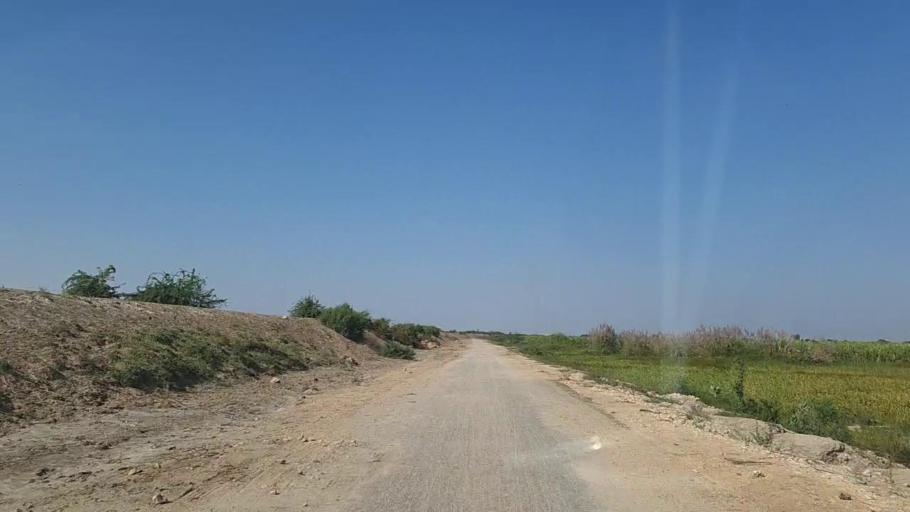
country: PK
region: Sindh
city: Chuhar Jamali
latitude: 24.5720
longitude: 68.0302
